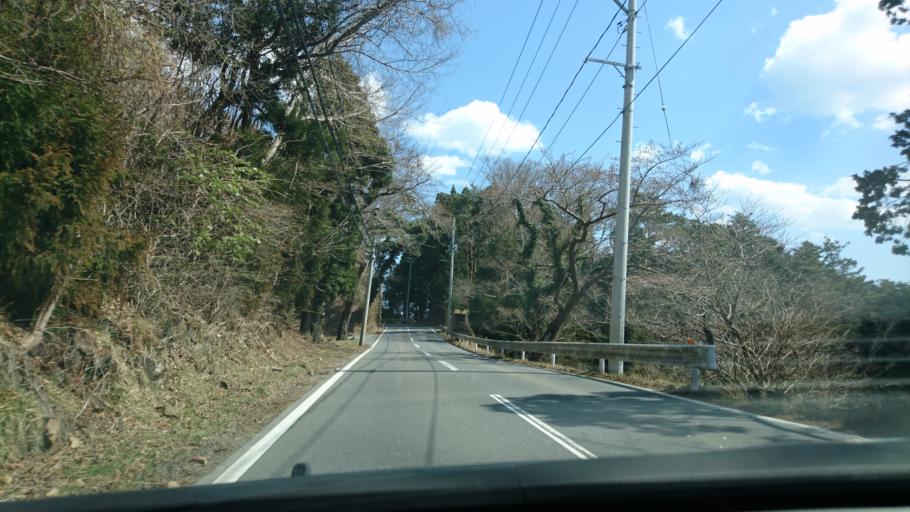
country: JP
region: Miyagi
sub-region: Oshika Gun
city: Onagawa Cho
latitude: 38.4394
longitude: 141.4814
